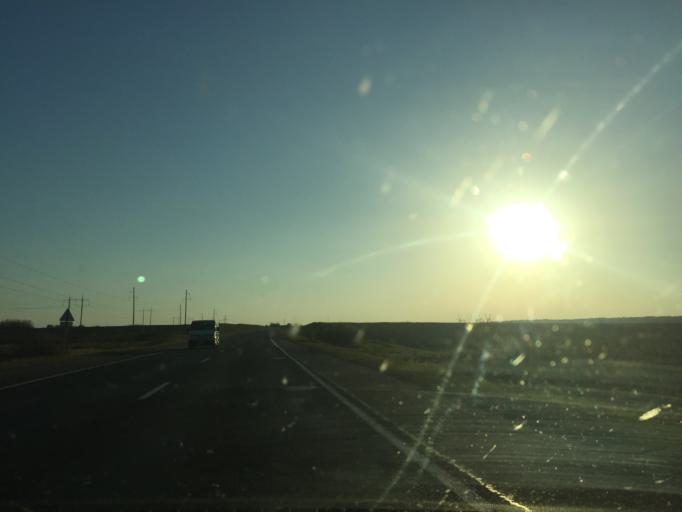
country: BY
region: Mogilev
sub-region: Mahilyowski Rayon
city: Veyno
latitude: 53.8018
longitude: 30.4452
